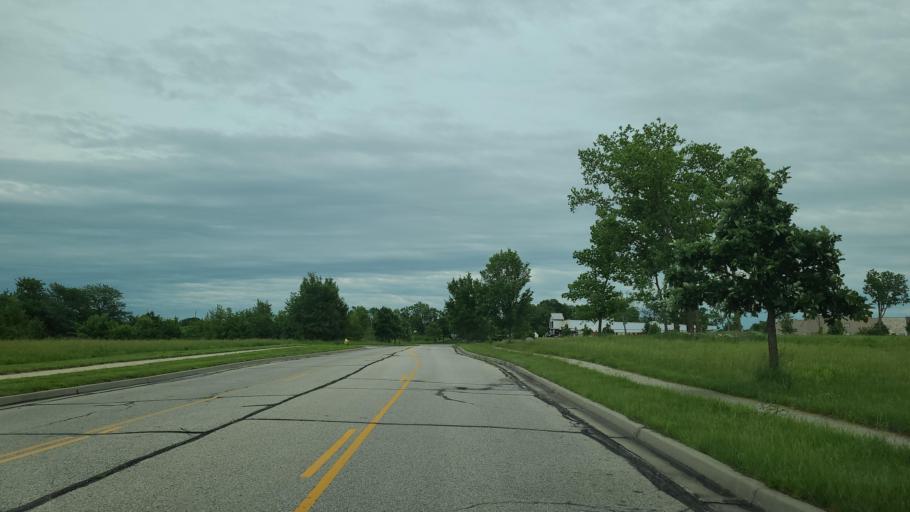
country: US
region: Kansas
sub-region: Douglas County
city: Lawrence
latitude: 38.9415
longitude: -95.2014
